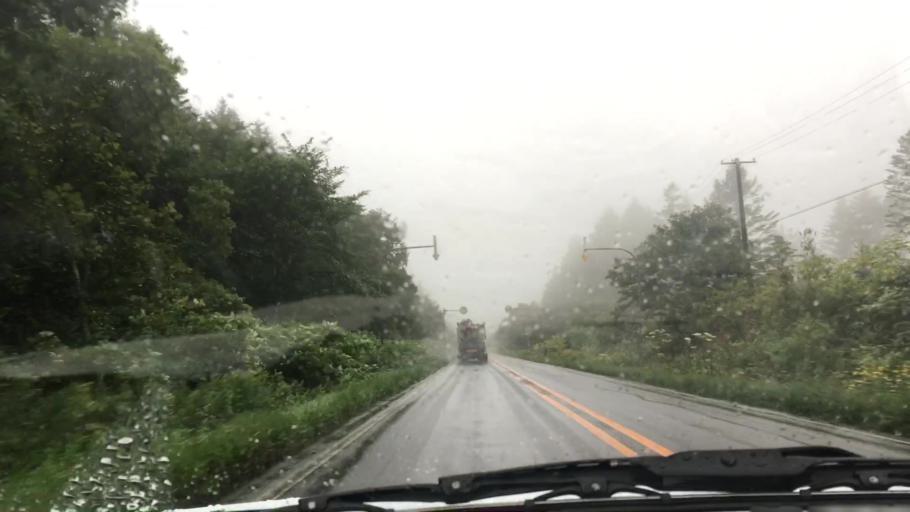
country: JP
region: Hokkaido
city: Niseko Town
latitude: 42.5934
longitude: 140.5118
